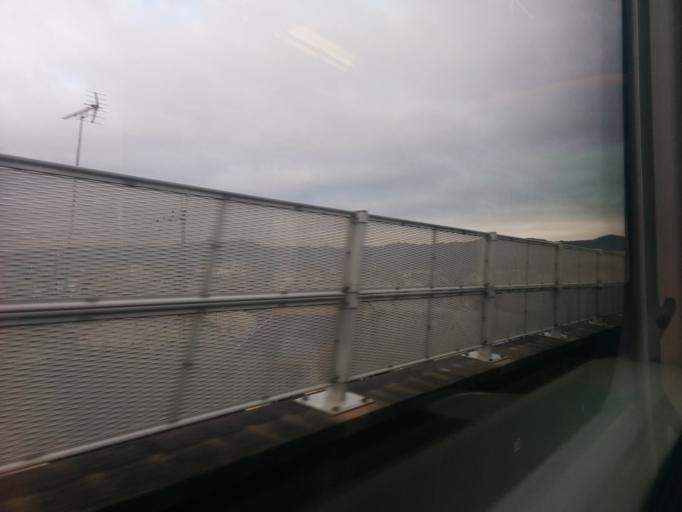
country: JP
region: Kyoto
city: Kyoto
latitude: 35.0188
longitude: 135.7255
